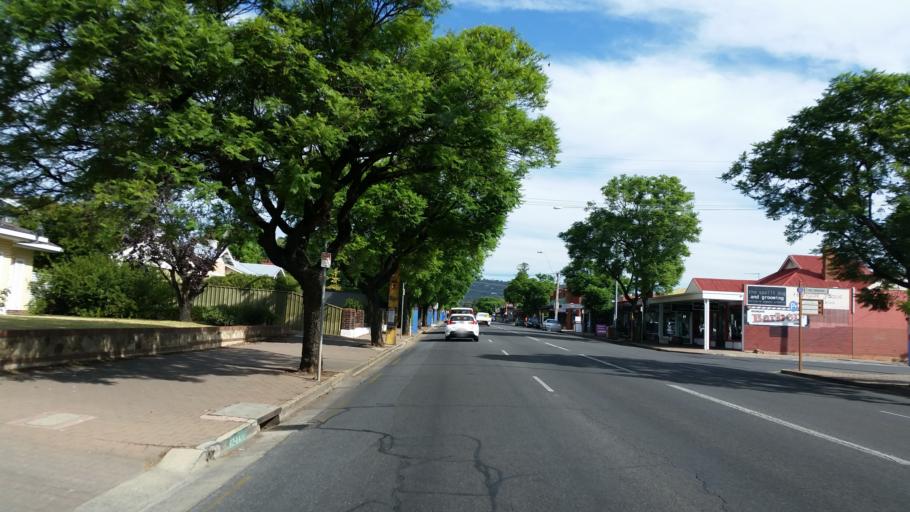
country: AU
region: South Australia
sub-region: Unley
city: Fullarton
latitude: -34.9586
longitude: 138.6260
